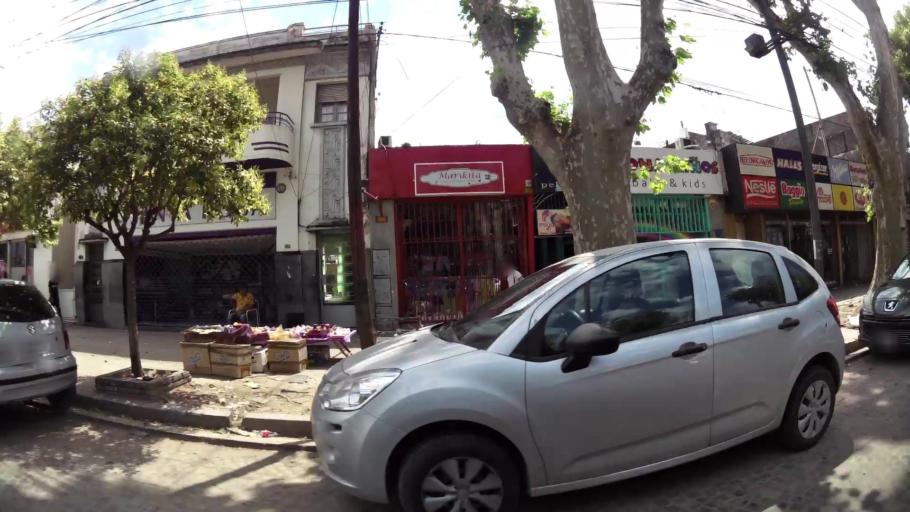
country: AR
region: Santa Fe
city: Gobernador Galvez
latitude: -32.9993
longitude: -60.6487
